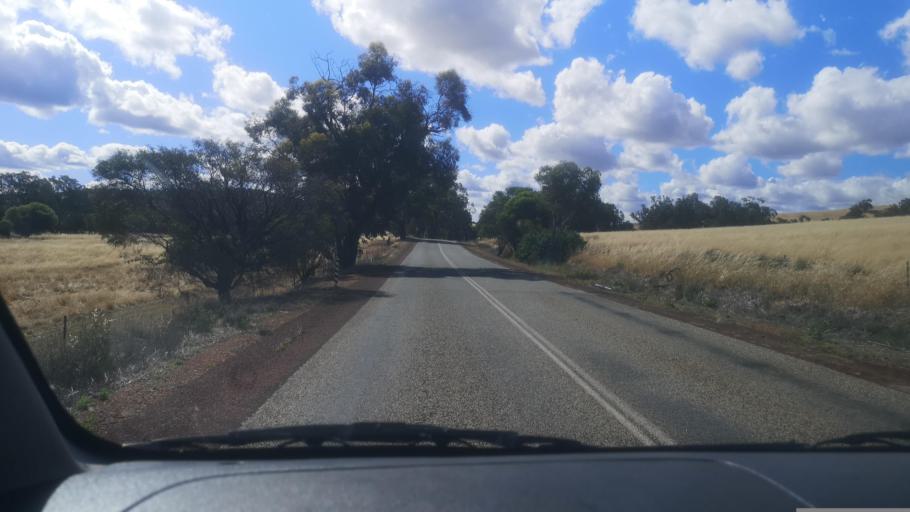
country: AU
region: Western Australia
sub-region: Toodyay
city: Toodyay
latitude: -31.5009
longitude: 116.4453
